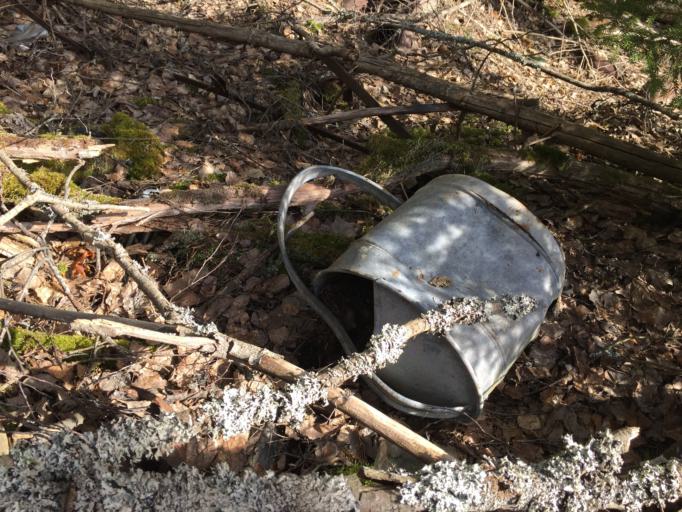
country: SE
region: Stockholm
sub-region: Salems Kommun
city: Ronninge
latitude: 59.2525
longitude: 17.6799
